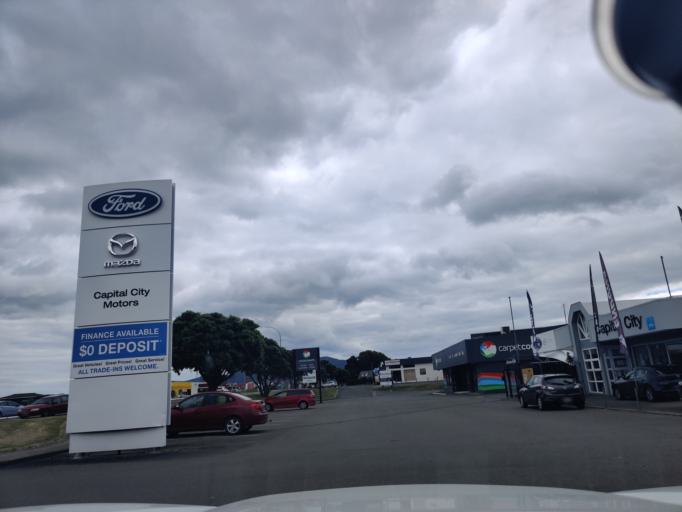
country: NZ
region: Wellington
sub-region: Kapiti Coast District
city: Paraparaumu
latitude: -40.9037
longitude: 174.9953
